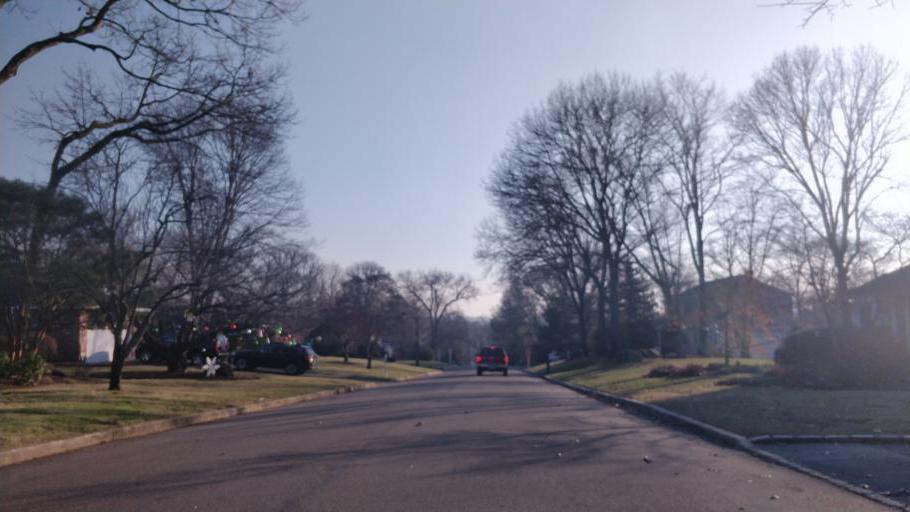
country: US
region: New York
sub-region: Nassau County
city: Bayville
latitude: 40.9033
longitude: -73.5664
